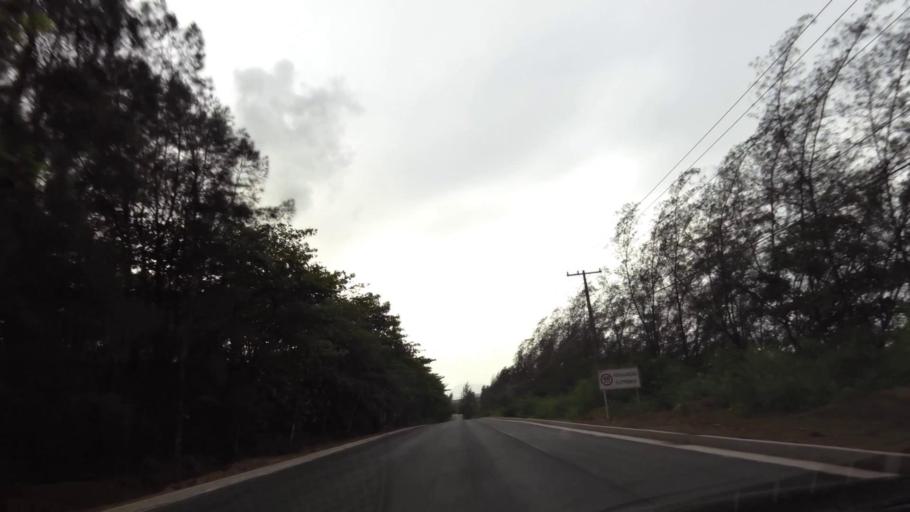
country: BR
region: Espirito Santo
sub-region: Guarapari
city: Guarapari
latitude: -20.7792
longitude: -40.5779
